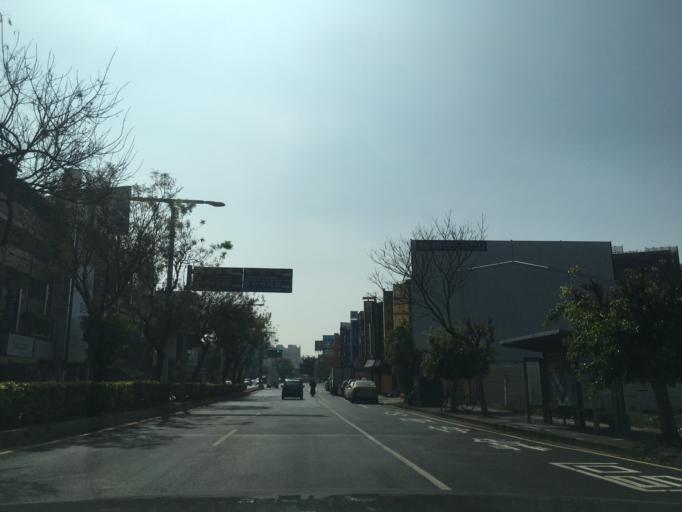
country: TW
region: Taiwan
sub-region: Taichung City
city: Taichung
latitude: 24.1943
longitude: 120.6589
